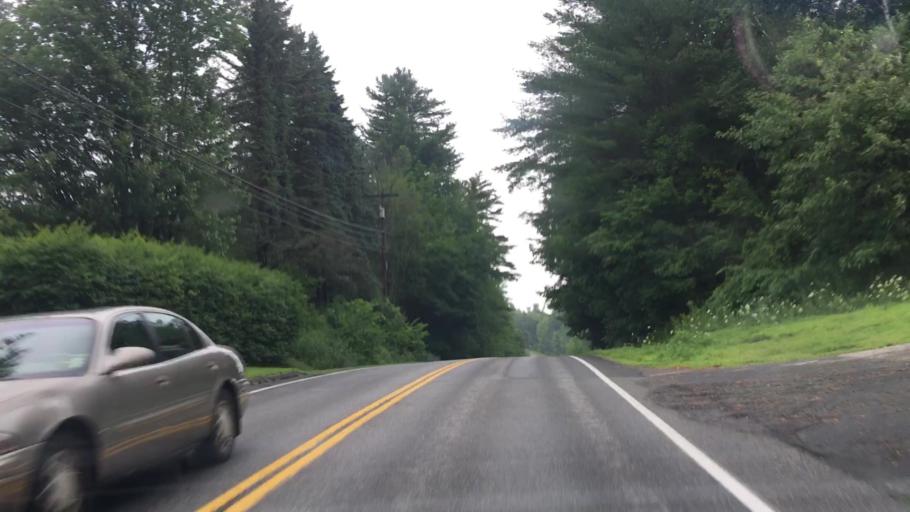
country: US
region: Maine
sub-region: Kennebec County
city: Augusta
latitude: 44.3373
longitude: -69.8131
